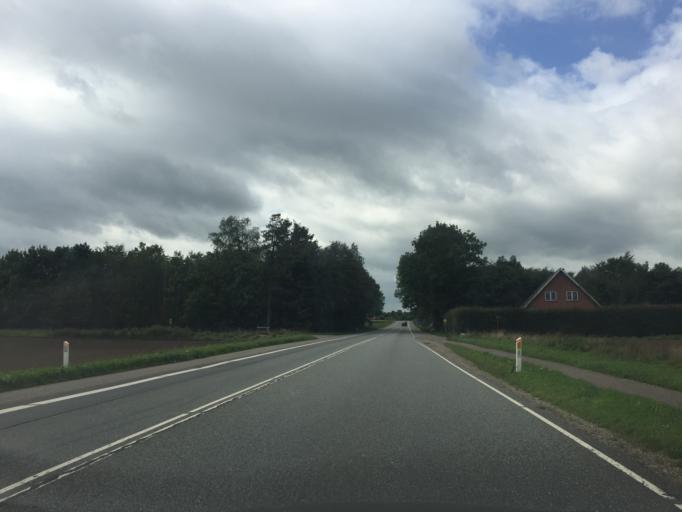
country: DK
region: Capital Region
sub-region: Hillerod Kommune
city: Skaevinge
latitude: 55.9419
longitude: 12.2060
